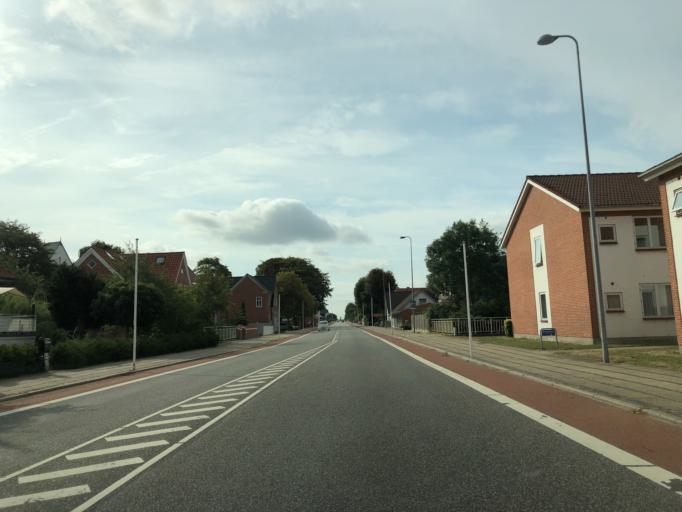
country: DK
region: Central Jutland
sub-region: Ringkobing-Skjern Kommune
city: Skjern
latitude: 55.9439
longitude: 8.4970
